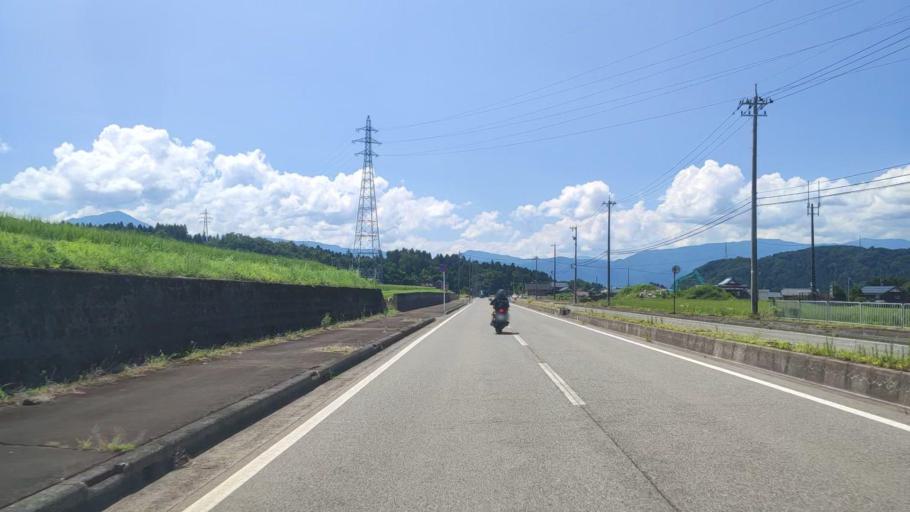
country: JP
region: Fukui
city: Katsuyama
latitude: 36.0361
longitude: 136.5200
